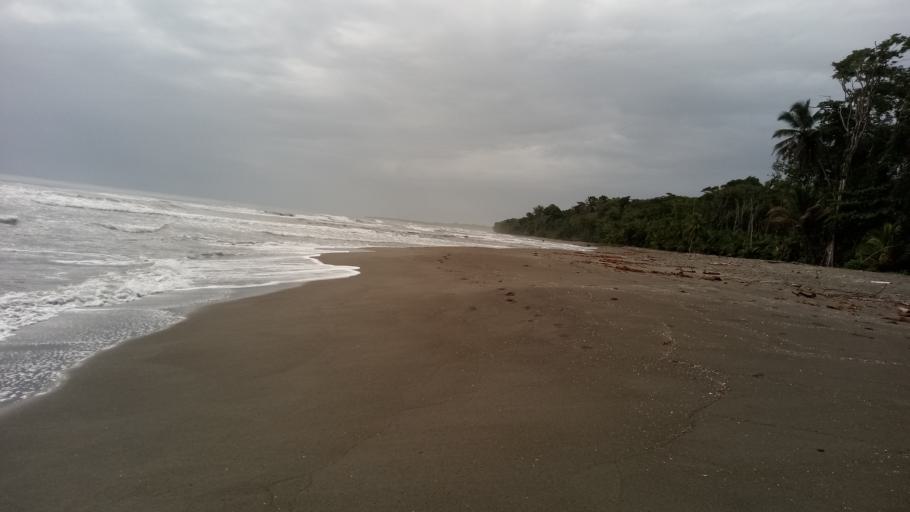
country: CR
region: Limon
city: Sixaola
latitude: 9.6155
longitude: -82.6200
